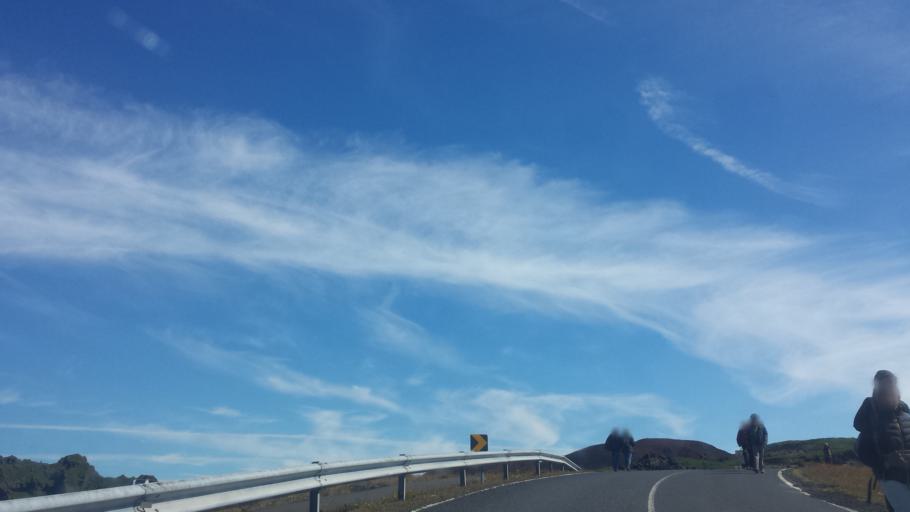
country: IS
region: South
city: Vestmannaeyjar
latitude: 63.4433
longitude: -20.2649
